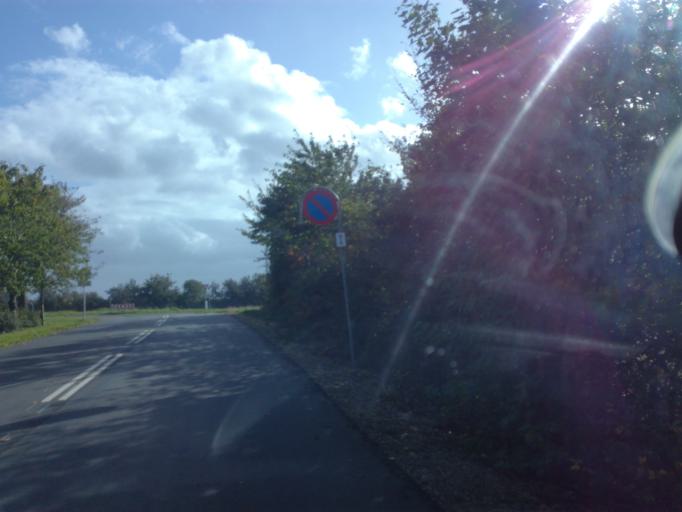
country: DK
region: South Denmark
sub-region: Fredericia Kommune
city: Fredericia
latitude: 55.5814
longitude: 9.7281
